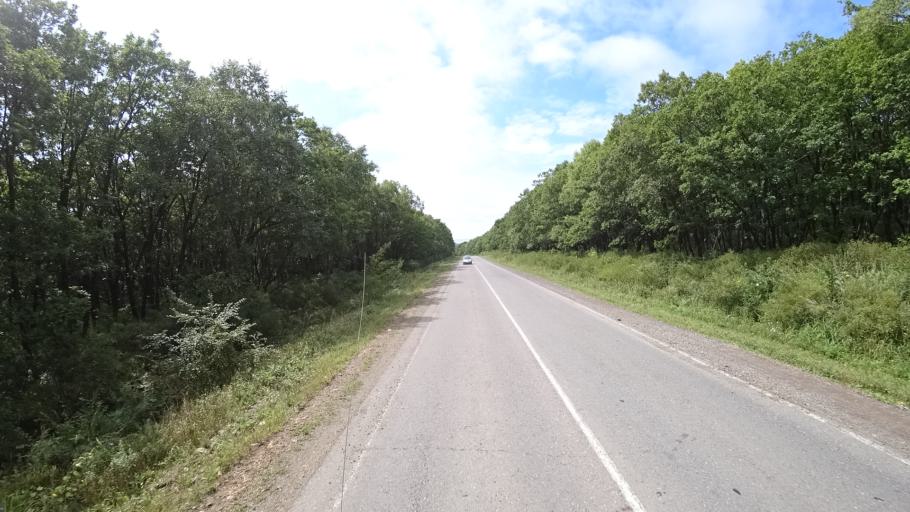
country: RU
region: Primorskiy
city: Lyalichi
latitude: 44.1397
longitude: 132.4196
